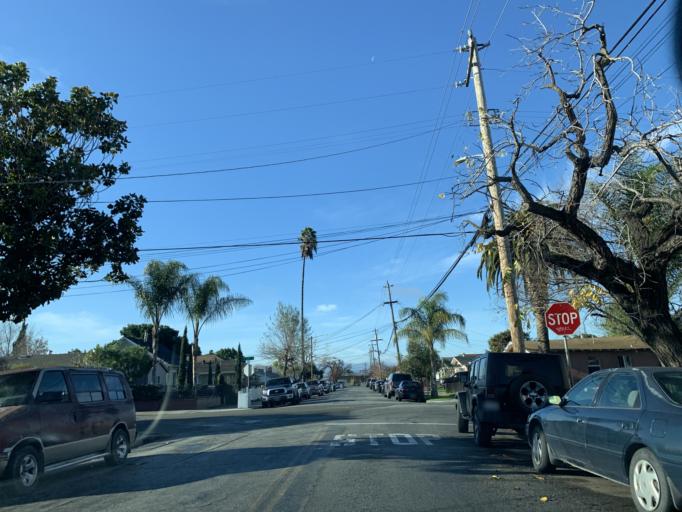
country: US
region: California
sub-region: Santa Clara County
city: Alum Rock
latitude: 37.3489
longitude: -121.8569
